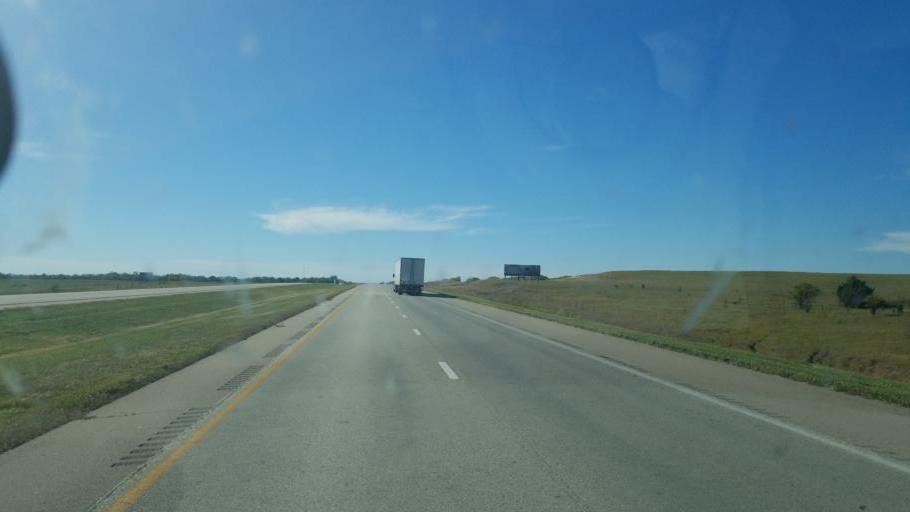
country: US
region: Kansas
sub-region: Saline County
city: Salina
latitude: 38.8781
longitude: -97.7295
